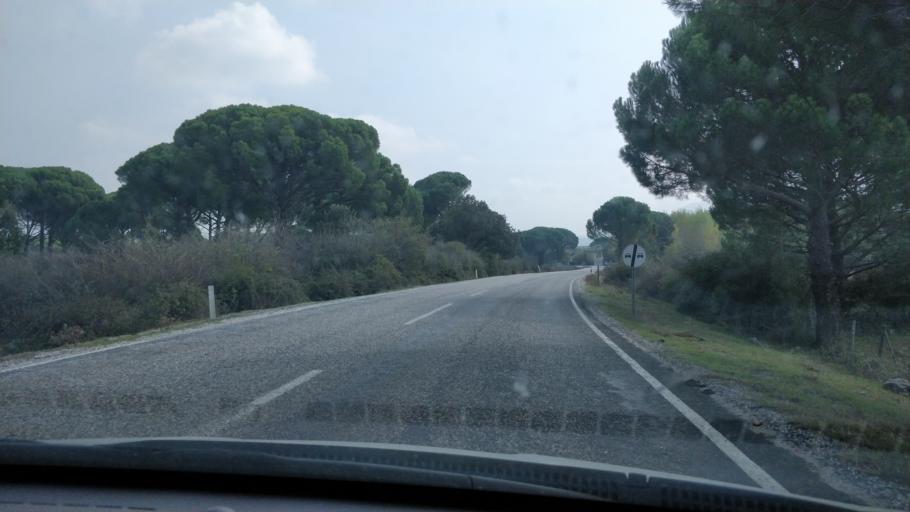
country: TR
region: Izmir
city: Kozak
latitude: 39.2604
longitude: 27.0360
